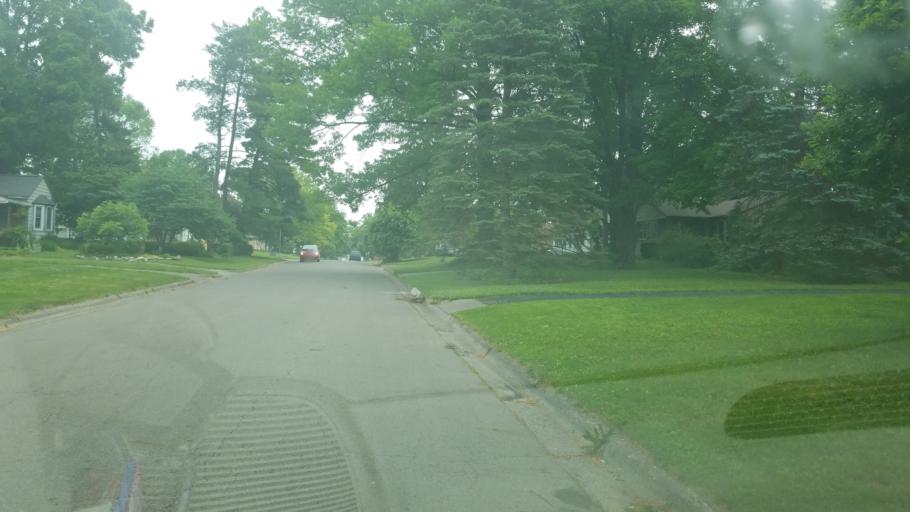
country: US
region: Ohio
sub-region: Franklin County
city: Worthington
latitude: 40.0582
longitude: -83.0069
